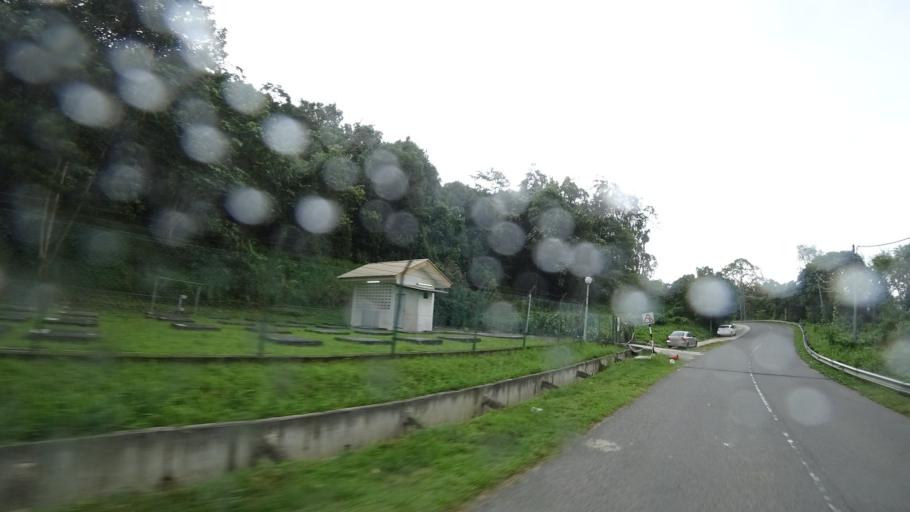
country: BN
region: Brunei and Muara
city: Bandar Seri Begawan
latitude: 4.8565
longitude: 114.9535
